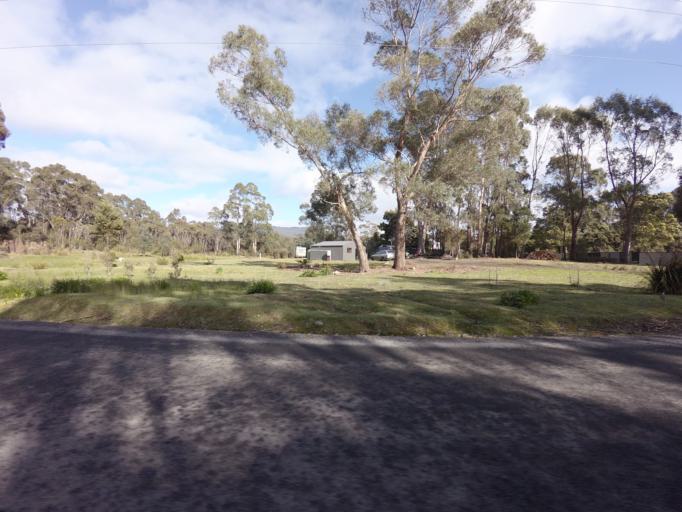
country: AU
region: Tasmania
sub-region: Huon Valley
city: Geeveston
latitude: -43.4314
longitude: 146.9035
